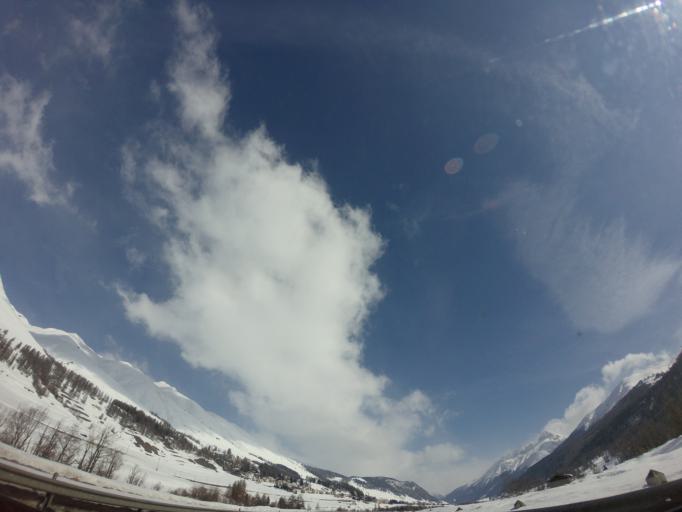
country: CH
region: Grisons
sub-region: Maloja District
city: Zuoz
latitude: 46.5878
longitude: 9.9457
